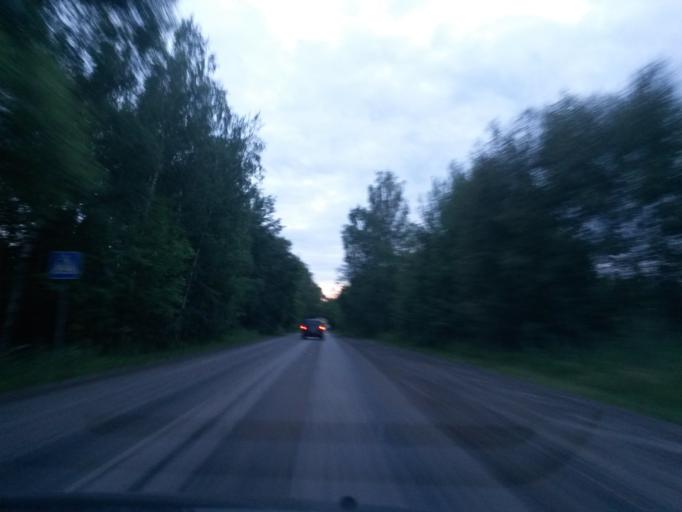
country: RU
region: Moskovskaya
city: Stolbovaya
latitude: 55.2446
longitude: 37.4721
